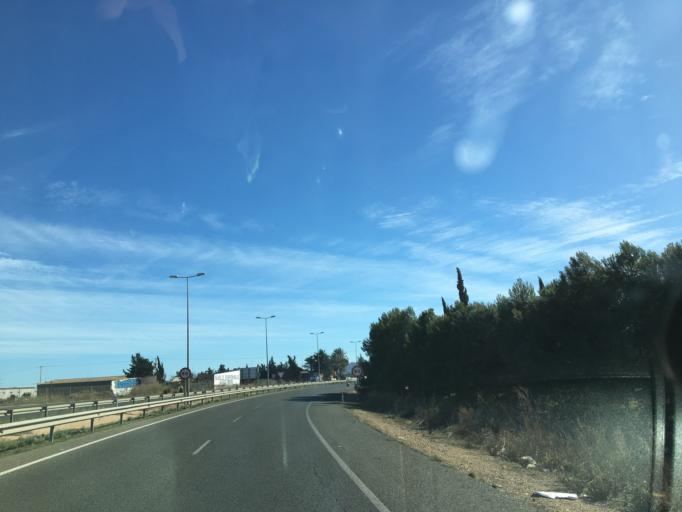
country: ES
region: Murcia
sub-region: Murcia
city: Cartagena
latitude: 37.6397
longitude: -0.9913
